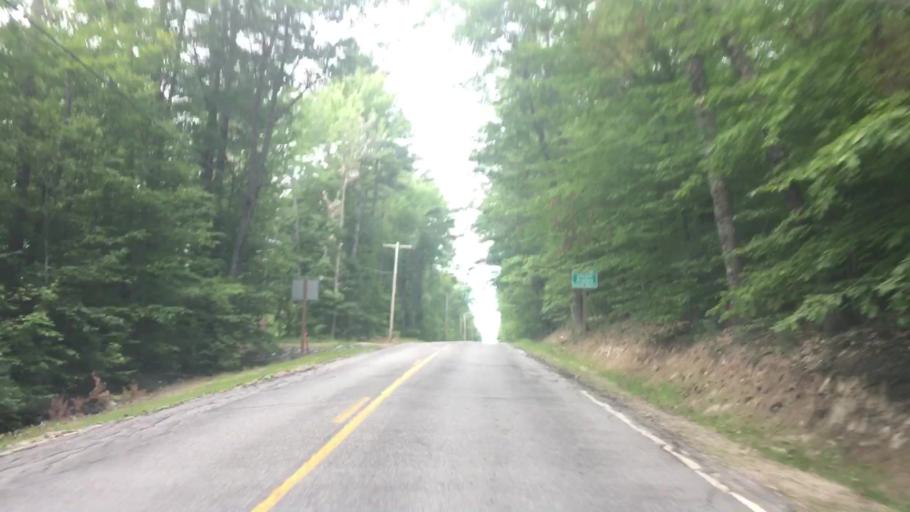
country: US
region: Maine
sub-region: Oxford County
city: Oxford
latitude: 44.0210
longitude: -70.5285
